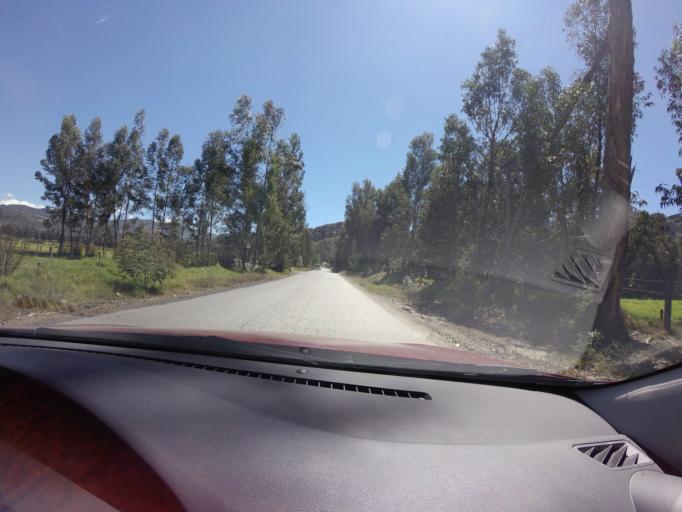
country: CO
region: Cundinamarca
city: Cucunuba
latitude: 5.2665
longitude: -73.7946
